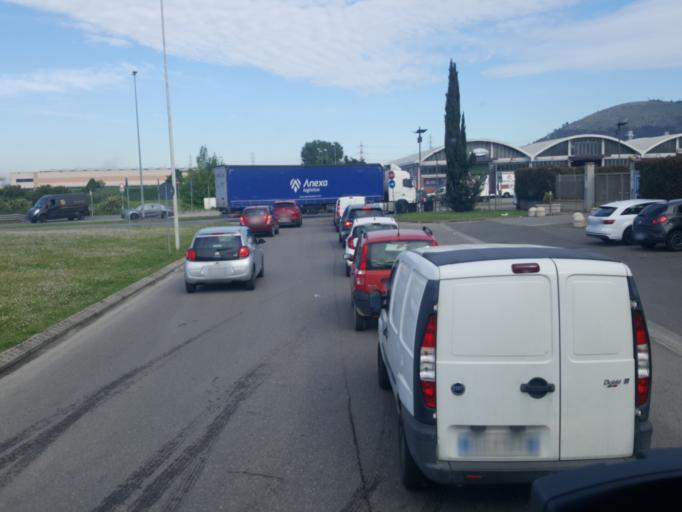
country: IT
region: Tuscany
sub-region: Province of Florence
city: Calenzano
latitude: 43.8440
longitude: 11.1595
